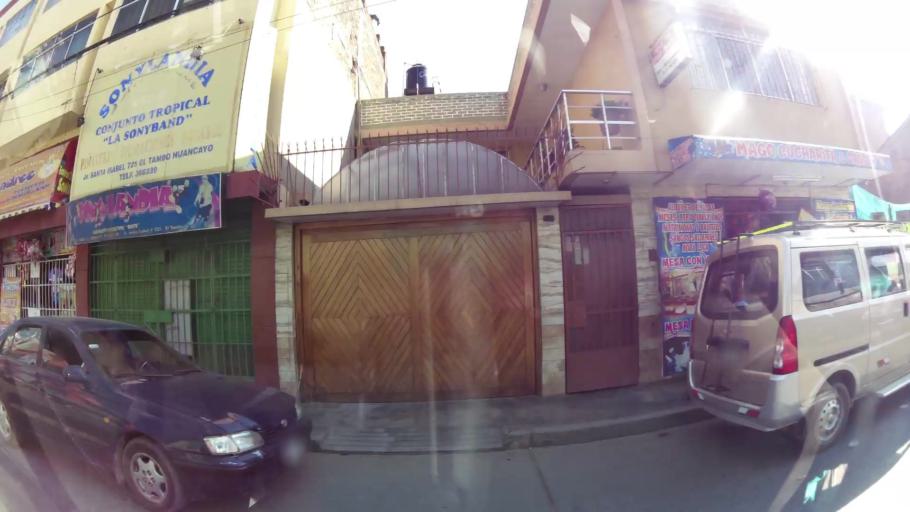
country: PE
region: Junin
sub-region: Provincia de Huancayo
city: El Tambo
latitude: -12.0588
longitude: -75.2139
